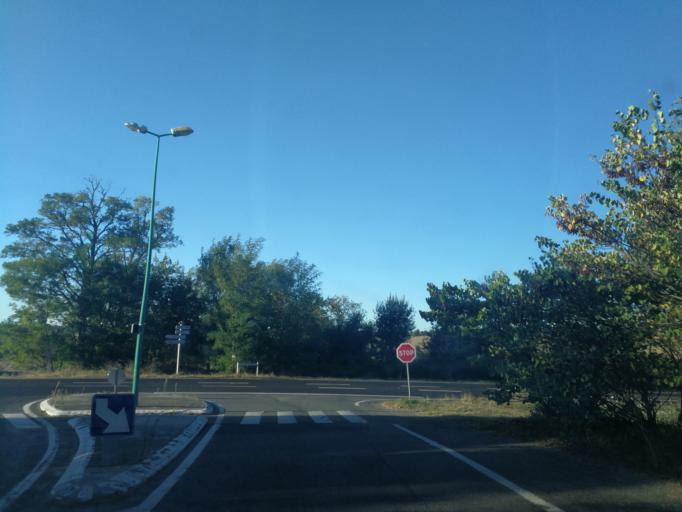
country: FR
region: Midi-Pyrenees
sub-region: Departement de la Haute-Garonne
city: Montrabe
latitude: 43.6329
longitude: 1.5086
